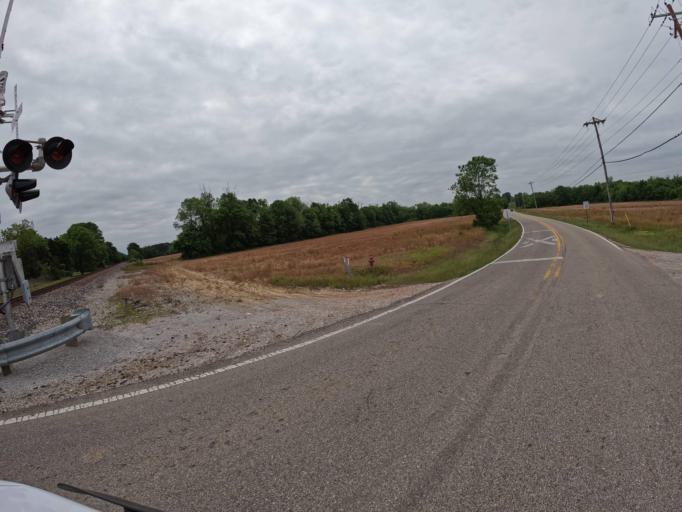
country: US
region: Mississippi
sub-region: Lee County
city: Tupelo
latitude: 34.2938
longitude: -88.7642
